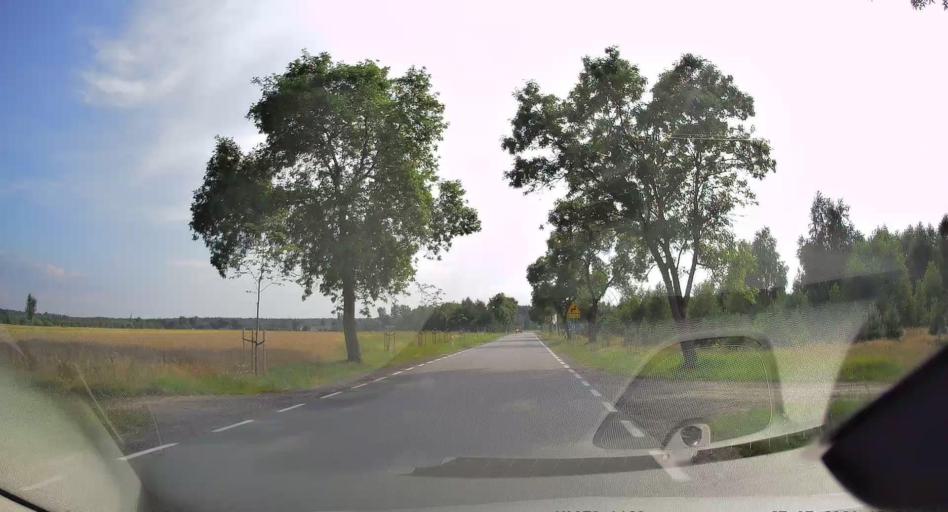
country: PL
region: Lodz Voivodeship
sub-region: Powiat tomaszowski
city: Rzeczyca
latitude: 51.5598
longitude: 20.2623
